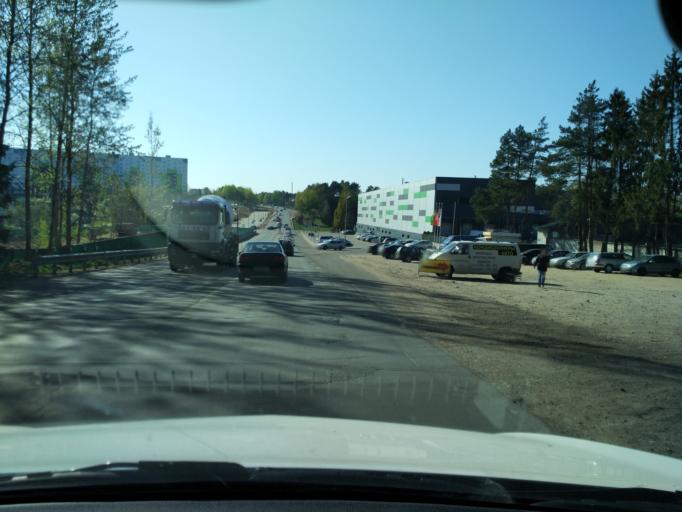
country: BY
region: Minsk
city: Borovlyany
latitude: 53.9637
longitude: 27.6755
